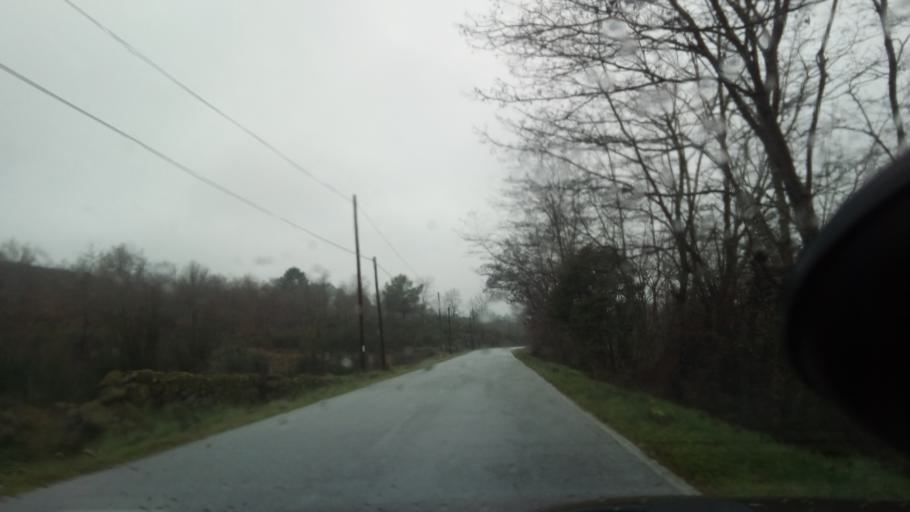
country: PT
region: Viseu
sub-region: Mangualde
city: Mangualde
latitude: 40.6114
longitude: -7.6624
